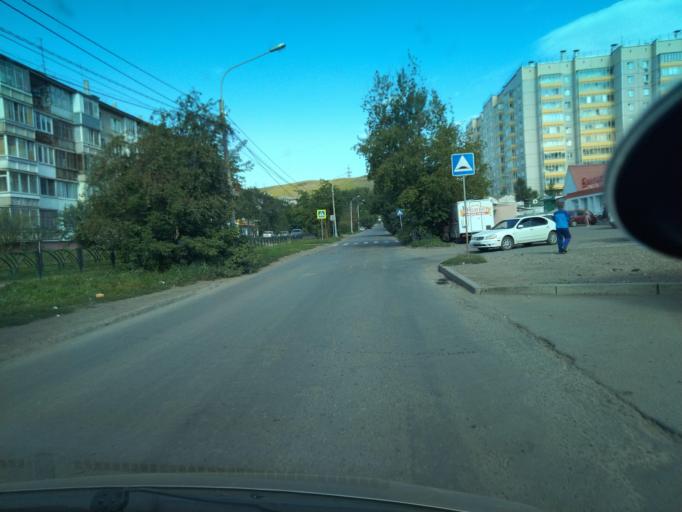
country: RU
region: Krasnoyarskiy
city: Krasnoyarsk
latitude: 55.9711
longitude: 92.9395
